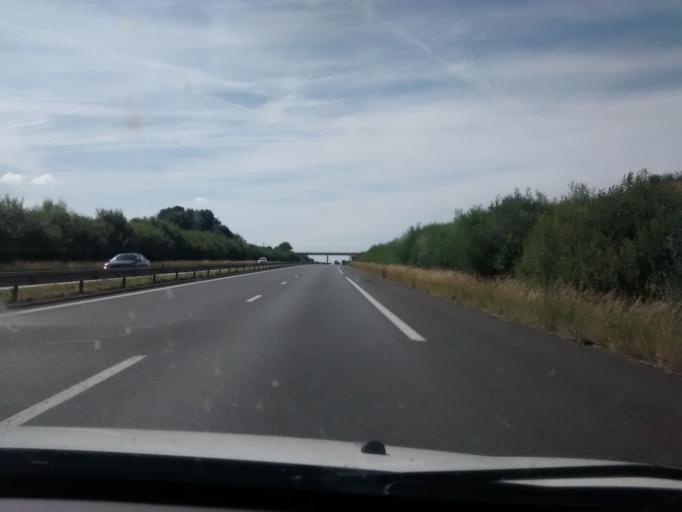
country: FR
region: Pays de la Loire
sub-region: Departement de la Mayenne
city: Argentre
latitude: 48.0859
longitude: -0.6711
